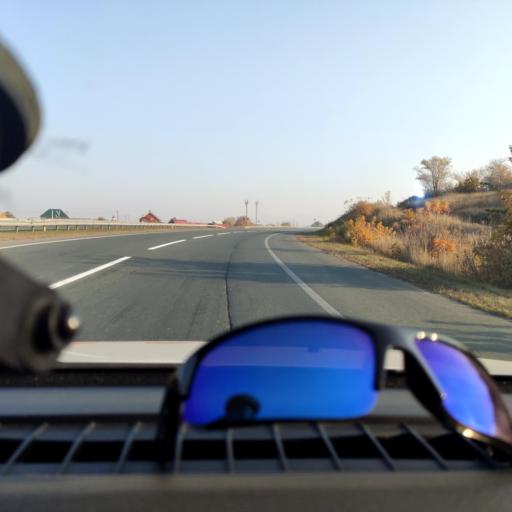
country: RU
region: Samara
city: Novokuybyshevsk
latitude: 53.0616
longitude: 50.0198
